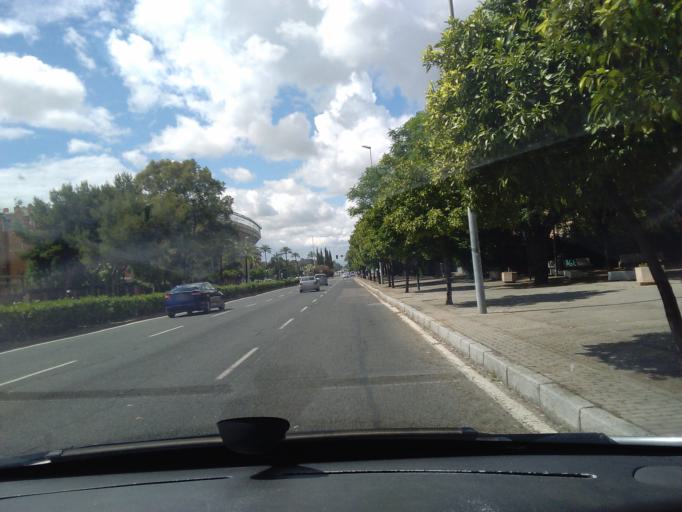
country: ES
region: Andalusia
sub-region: Provincia de Sevilla
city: Sevilla
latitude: 37.3545
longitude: -5.9788
